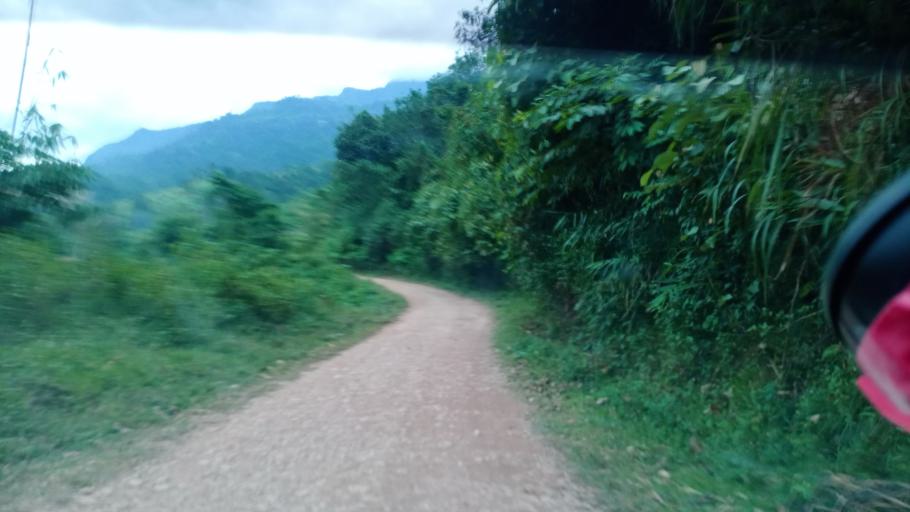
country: TH
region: Changwat Bueng Kan
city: Pak Khat
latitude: 18.7145
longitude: 103.2151
